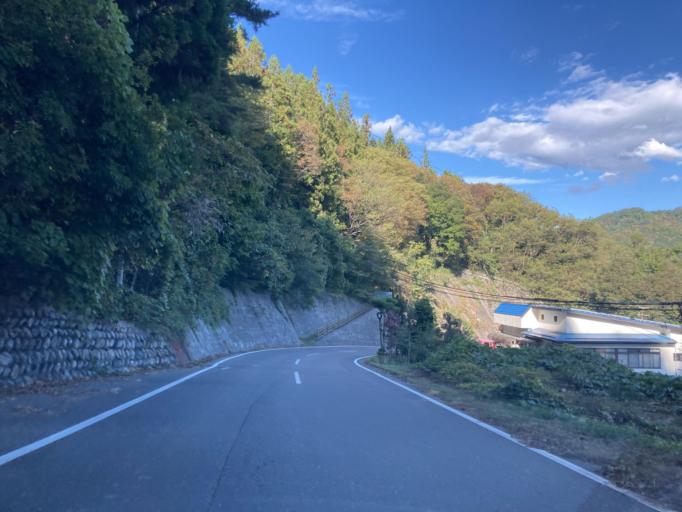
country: JP
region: Nagano
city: Omachi
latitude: 36.4921
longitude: 137.9112
